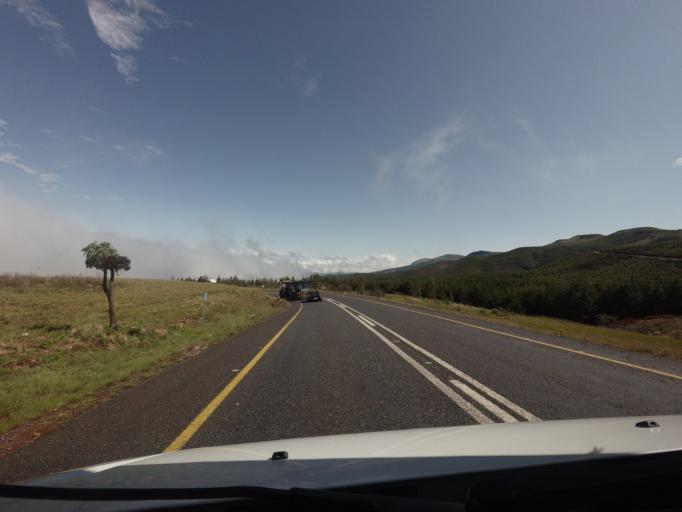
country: ZA
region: Mpumalanga
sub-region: Ehlanzeni District
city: Lydenburg
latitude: -25.1635
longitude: 30.6276
